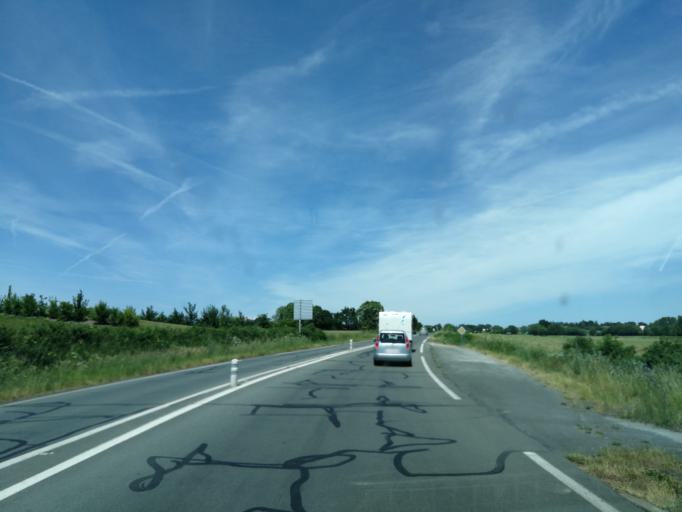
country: FR
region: Pays de la Loire
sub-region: Departement de la Vendee
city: La Tardiere
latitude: 46.6642
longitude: -0.7277
